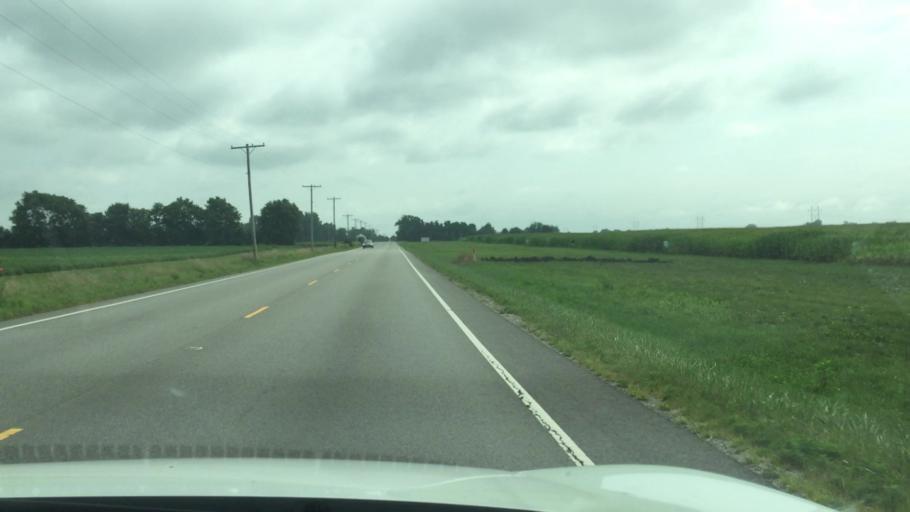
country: US
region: Ohio
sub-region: Union County
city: Marysville
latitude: 40.1646
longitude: -83.4474
